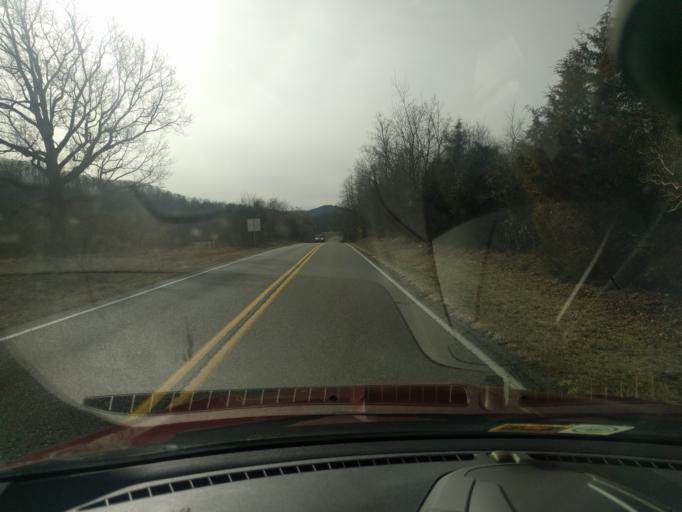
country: US
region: Virginia
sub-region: Augusta County
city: Stuarts Draft
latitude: 38.0247
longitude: -79.1356
